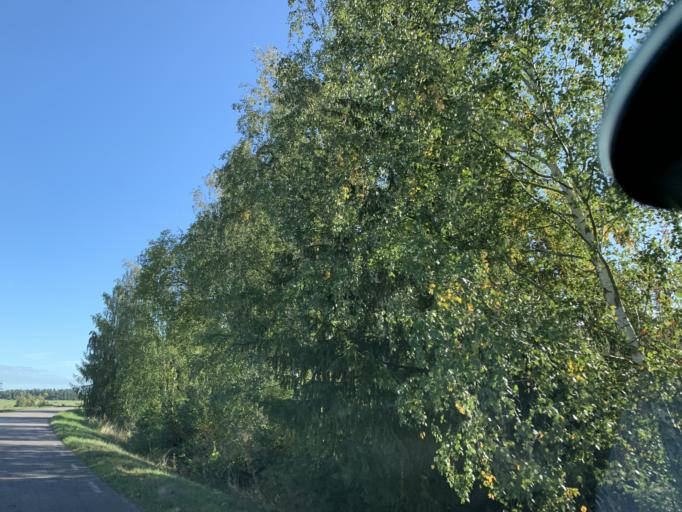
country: SE
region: Soedermanland
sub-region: Eskilstuna Kommun
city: Kvicksund
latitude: 59.5457
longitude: 16.4014
